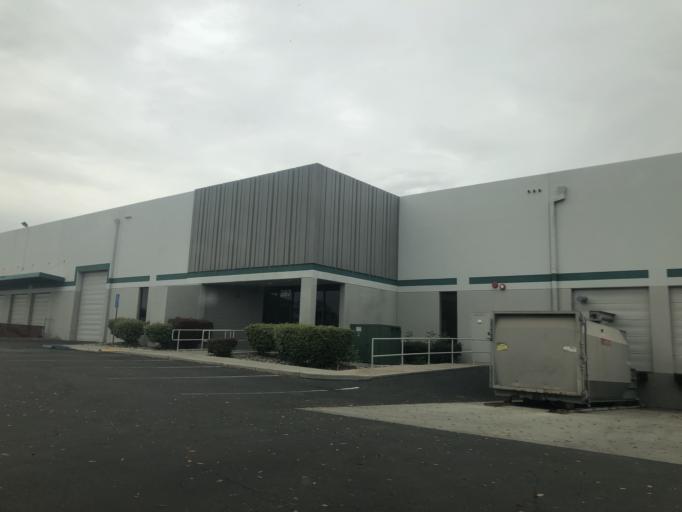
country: US
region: California
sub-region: Santa Clara County
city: San Jose
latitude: 37.3789
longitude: -121.9127
